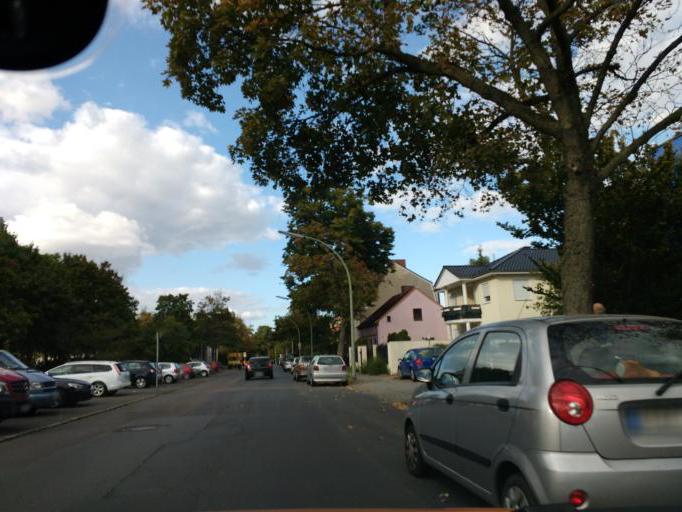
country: DE
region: Berlin
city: Britz
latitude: 52.4178
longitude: 13.4382
